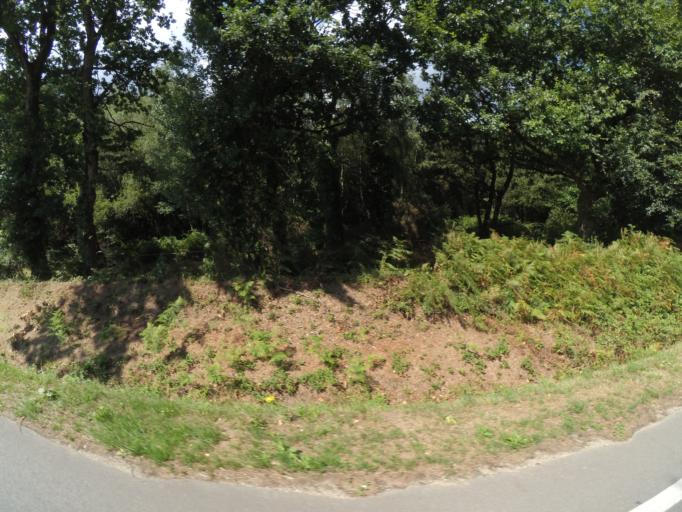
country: FR
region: Brittany
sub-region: Departement du Morbihan
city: Nostang
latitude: 47.7506
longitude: -3.1681
